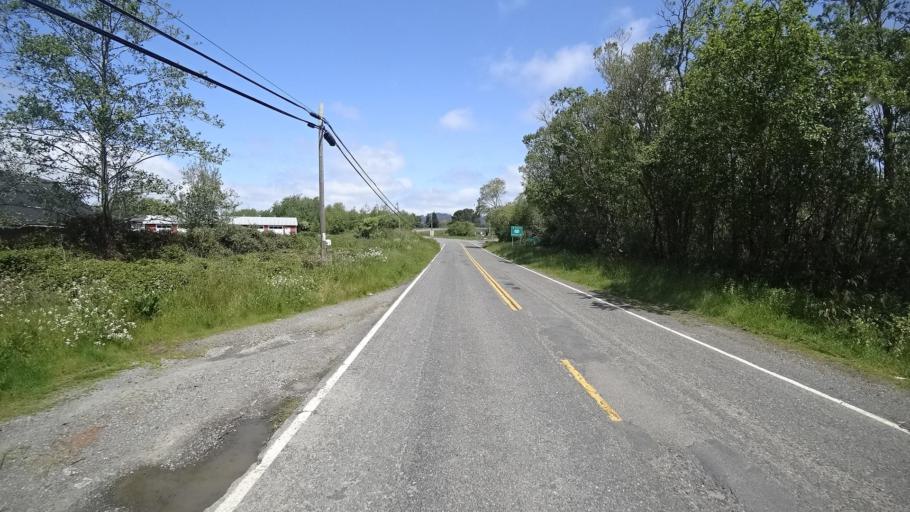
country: US
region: California
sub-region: Humboldt County
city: Humboldt Hill
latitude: 40.6689
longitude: -124.2031
